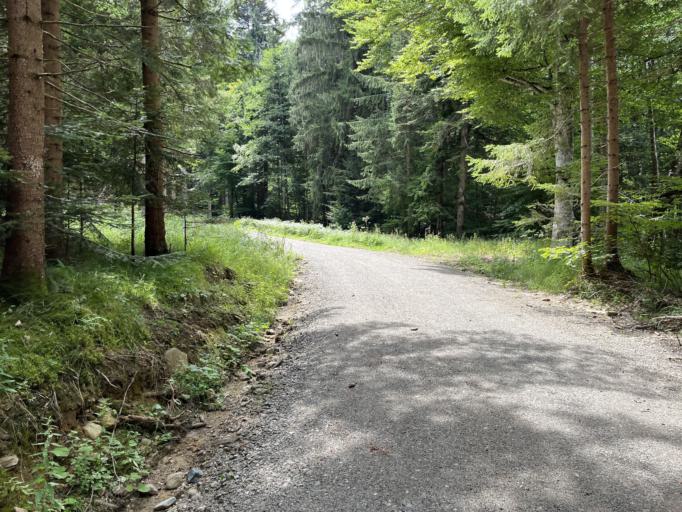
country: AT
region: Carinthia
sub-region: Politischer Bezirk Spittal an der Drau
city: Millstatt
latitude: 46.7956
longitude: 13.5467
